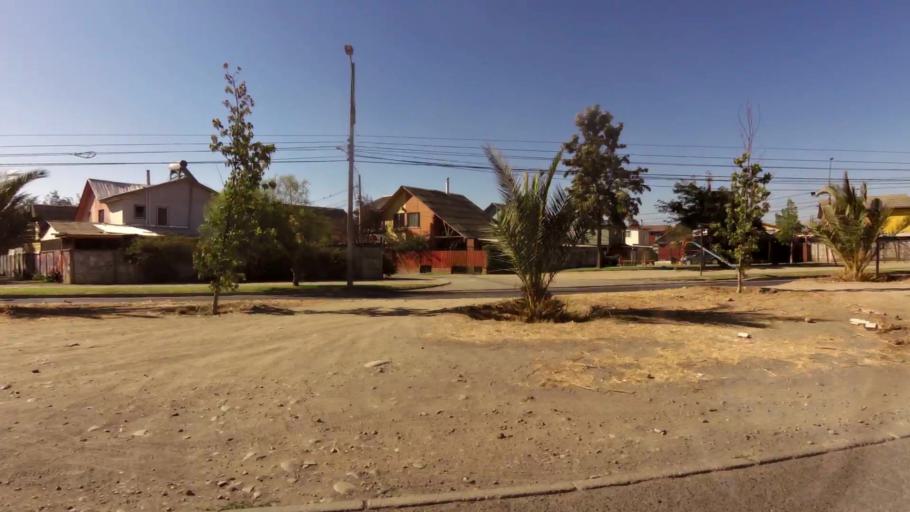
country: CL
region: O'Higgins
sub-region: Provincia de Cachapoal
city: Rancagua
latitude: -34.1793
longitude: -70.7664
